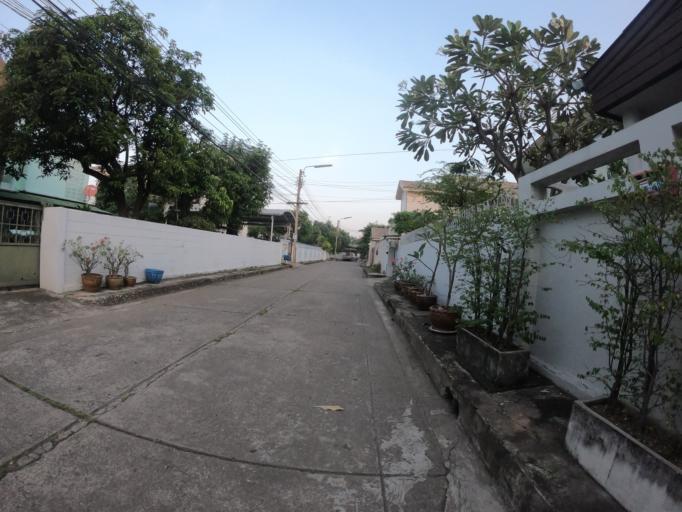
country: TH
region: Bangkok
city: Lat Phrao
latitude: 13.8298
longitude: 100.6064
